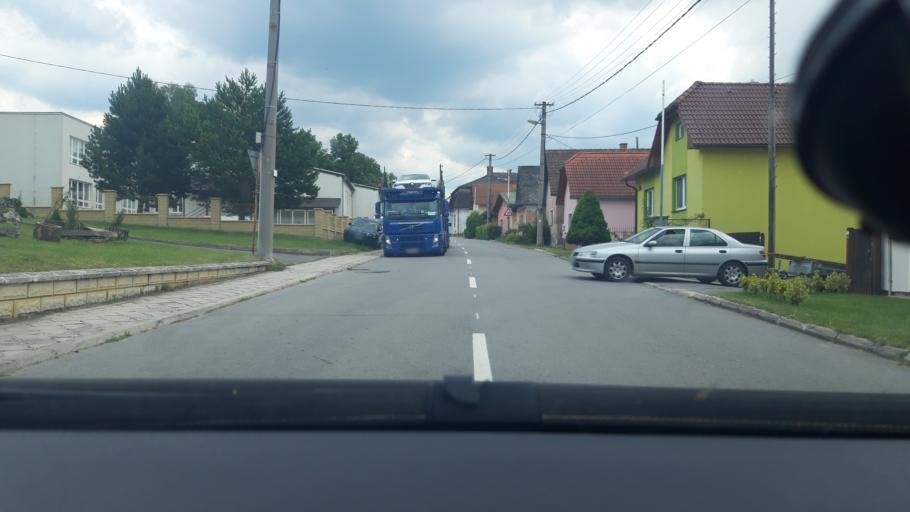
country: SK
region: Zilinsky
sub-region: Okres Martin
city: Martin
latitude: 48.9112
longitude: 18.8862
